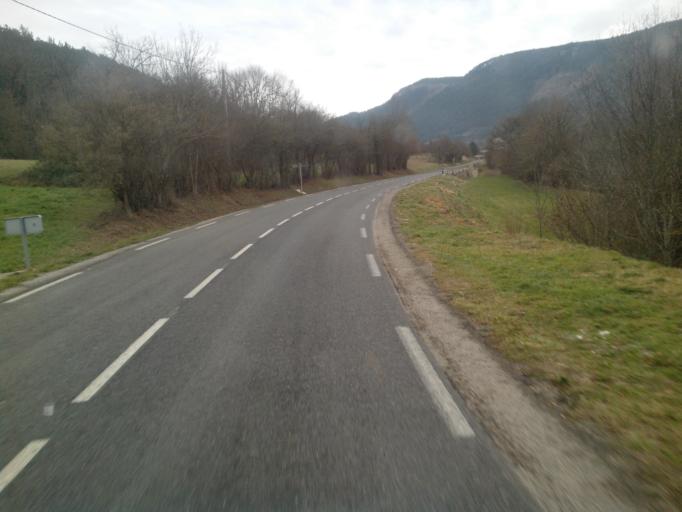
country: FR
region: Languedoc-Roussillon
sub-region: Departement de la Lozere
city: Mende
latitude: 44.4640
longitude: 3.5174
